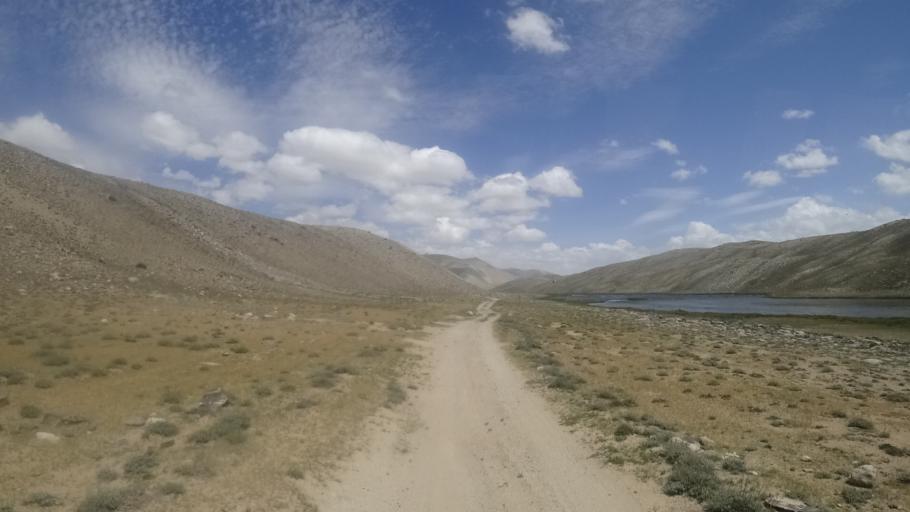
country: TJ
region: Gorno-Badakhshan
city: Murghob
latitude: 37.4714
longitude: 73.4357
